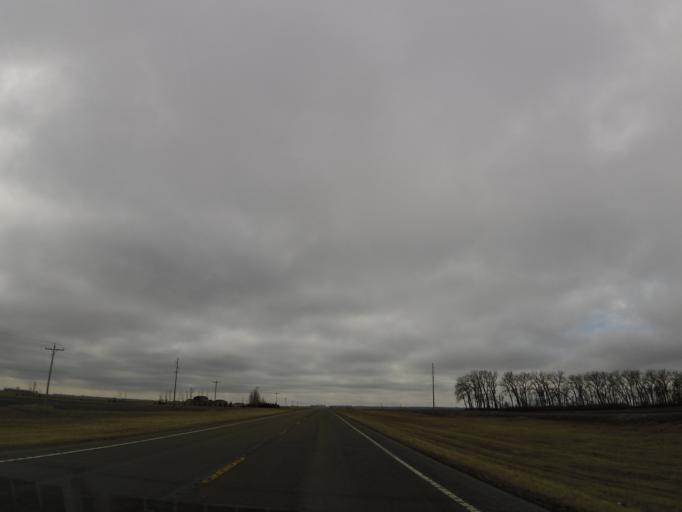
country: US
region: North Dakota
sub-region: Cass County
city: Casselton
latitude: 47.0676
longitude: -97.2183
